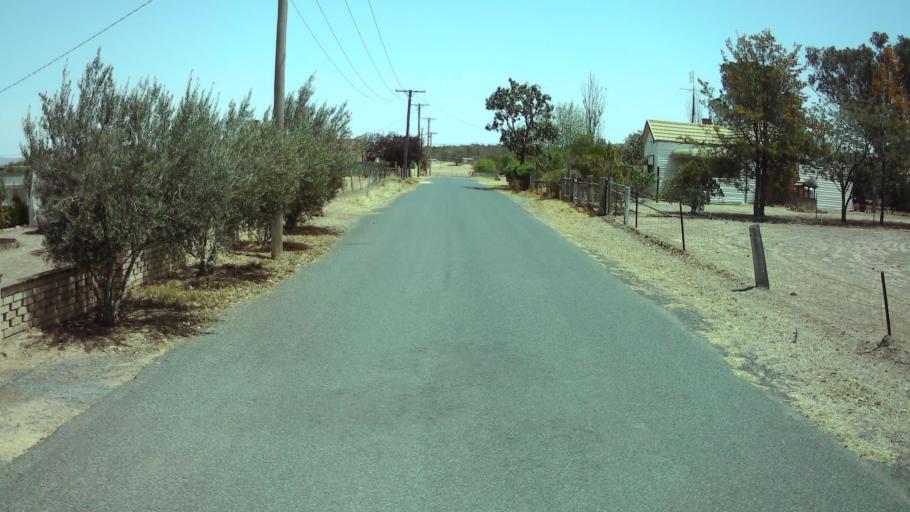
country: AU
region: New South Wales
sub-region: Weddin
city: Grenfell
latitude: -33.8881
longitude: 148.1643
